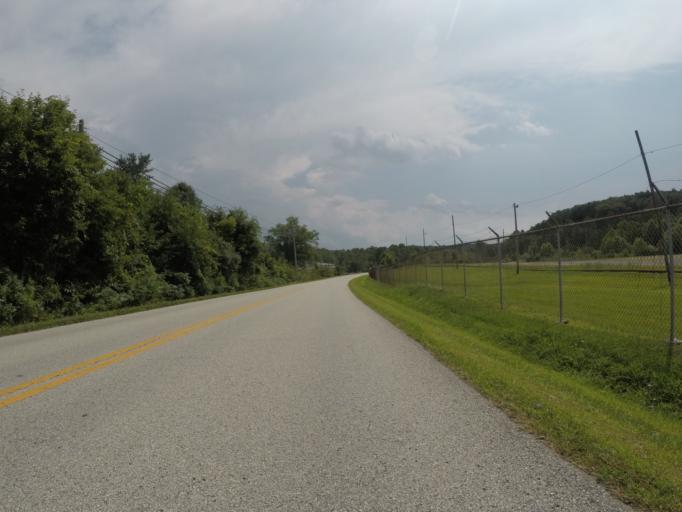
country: US
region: Kentucky
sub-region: Boyd County
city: Ironville
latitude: 38.4453
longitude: -82.7008
